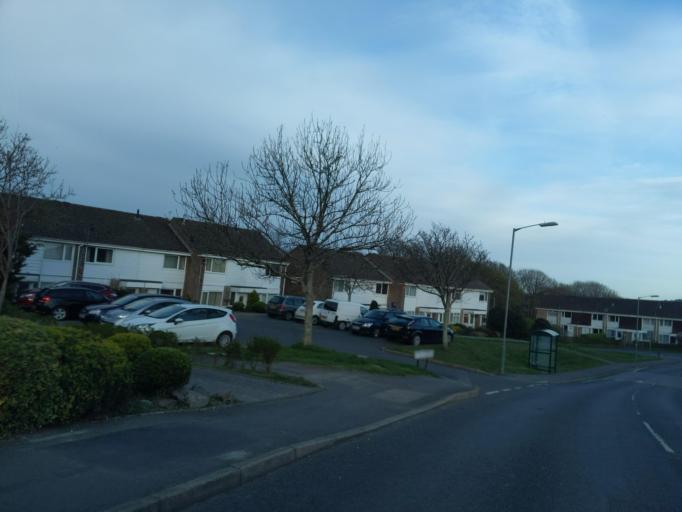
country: GB
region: England
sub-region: Cornwall
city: Torpoint
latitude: 50.3753
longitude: -4.2133
